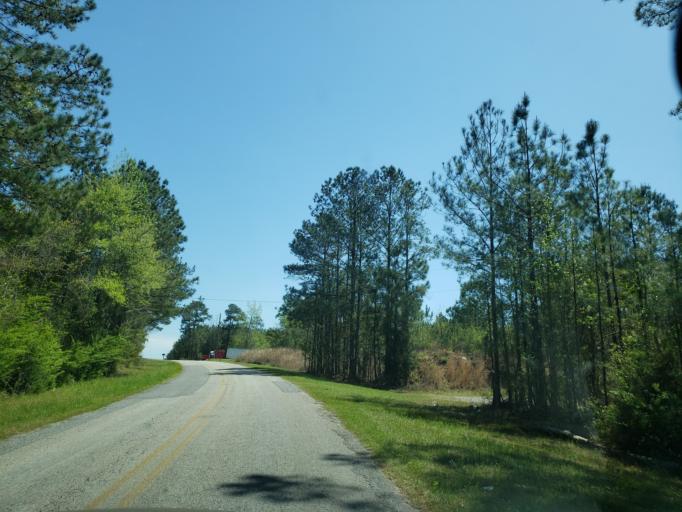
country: US
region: Alabama
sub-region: Tallapoosa County
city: Camp Hill
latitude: 32.6675
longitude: -85.7286
